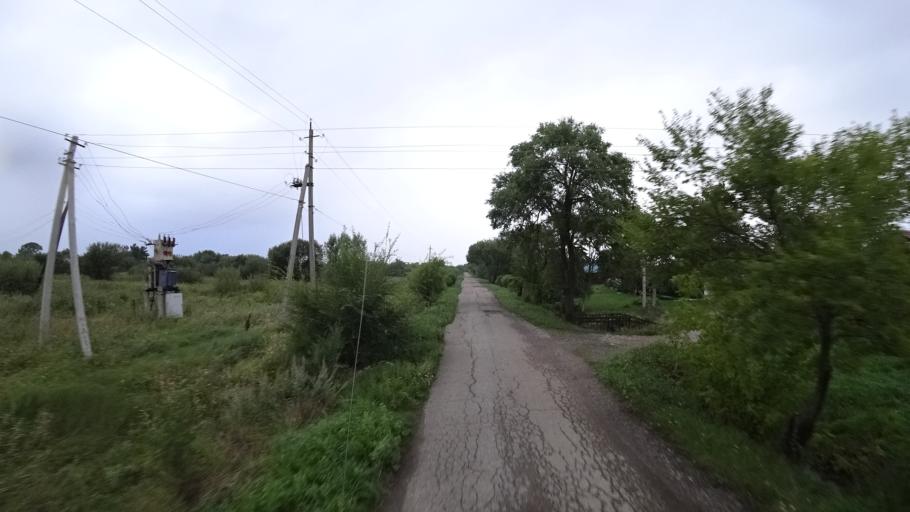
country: RU
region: Primorskiy
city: Chernigovka
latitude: 44.3996
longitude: 132.5313
